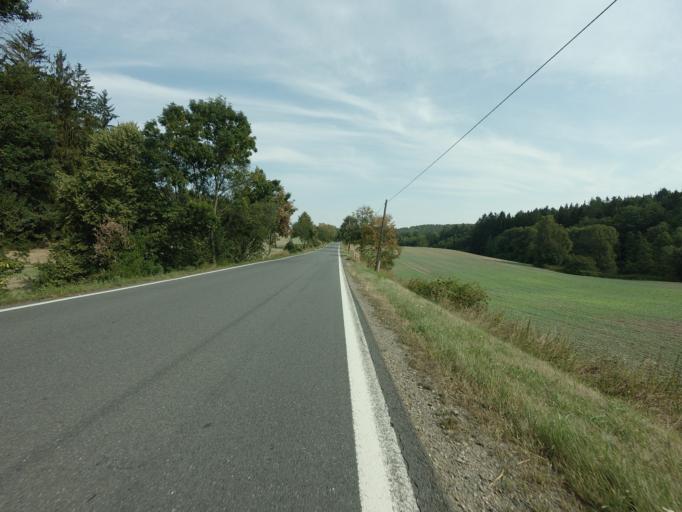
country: CZ
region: Central Bohemia
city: Petrovice
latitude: 49.5259
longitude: 14.3546
